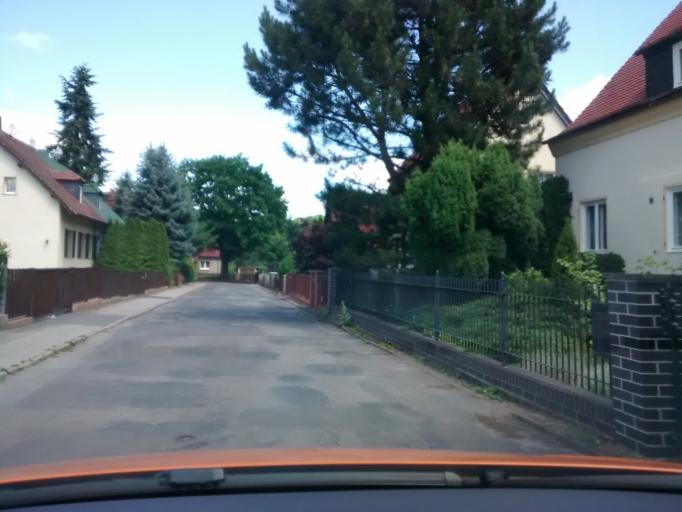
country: DE
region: Brandenburg
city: Potsdam
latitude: 52.3697
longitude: 13.0850
